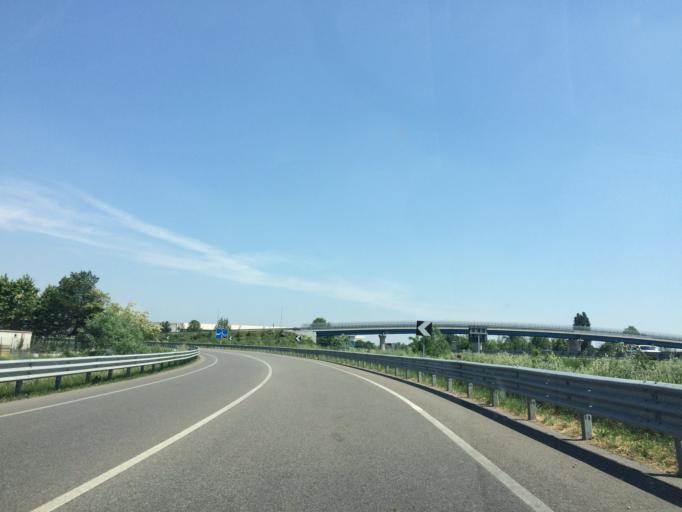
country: IT
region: Lombardy
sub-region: Provincia di Brescia
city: Flero
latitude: 45.4761
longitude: 10.1738
